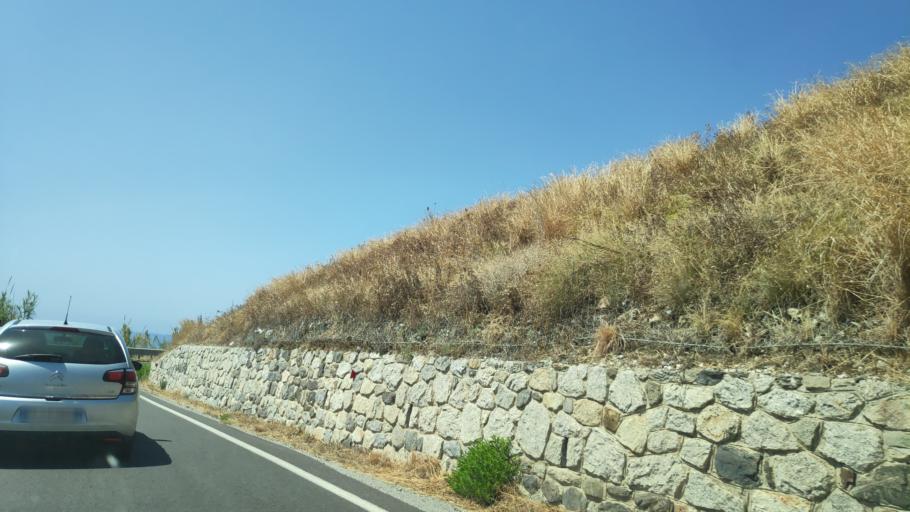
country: IT
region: Calabria
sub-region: Provincia di Reggio Calabria
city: Palizzi Marina
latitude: 37.9170
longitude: 15.9991
